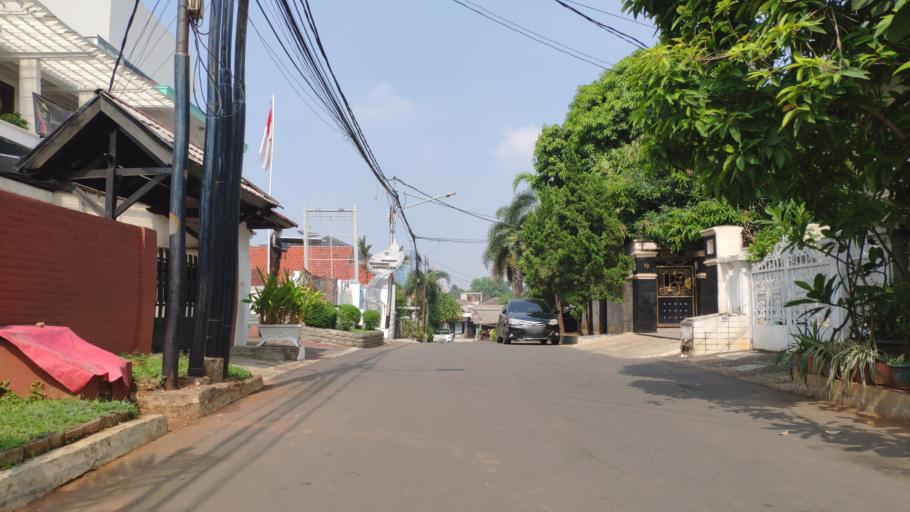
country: ID
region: Banten
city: South Tangerang
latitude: -6.2896
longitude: 106.7936
